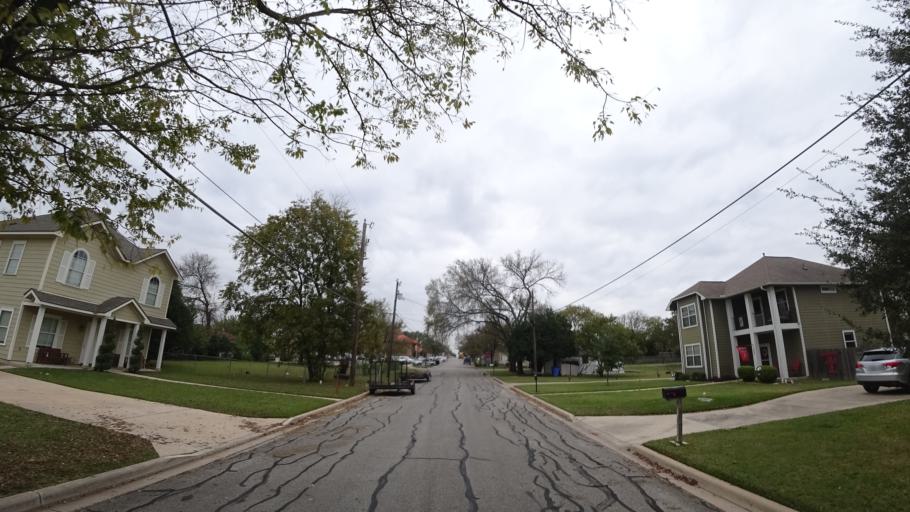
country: US
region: Texas
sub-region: Travis County
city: Pflugerville
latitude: 30.4422
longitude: -97.6195
